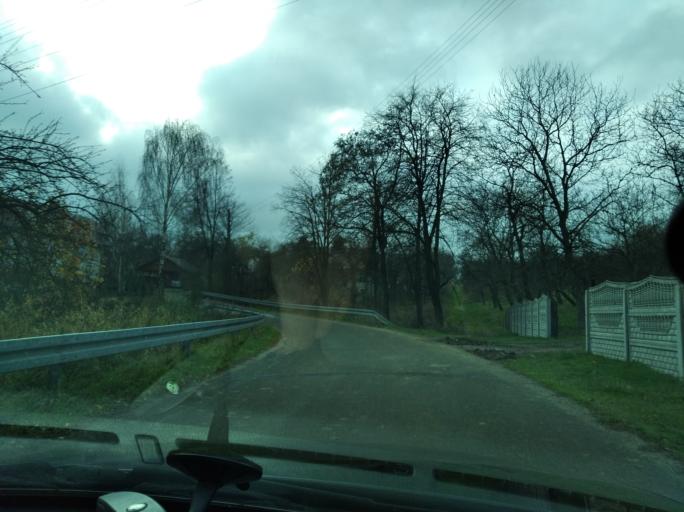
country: PL
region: Subcarpathian Voivodeship
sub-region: Powiat przeworski
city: Sietesz
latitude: 49.9726
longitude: 22.3380
